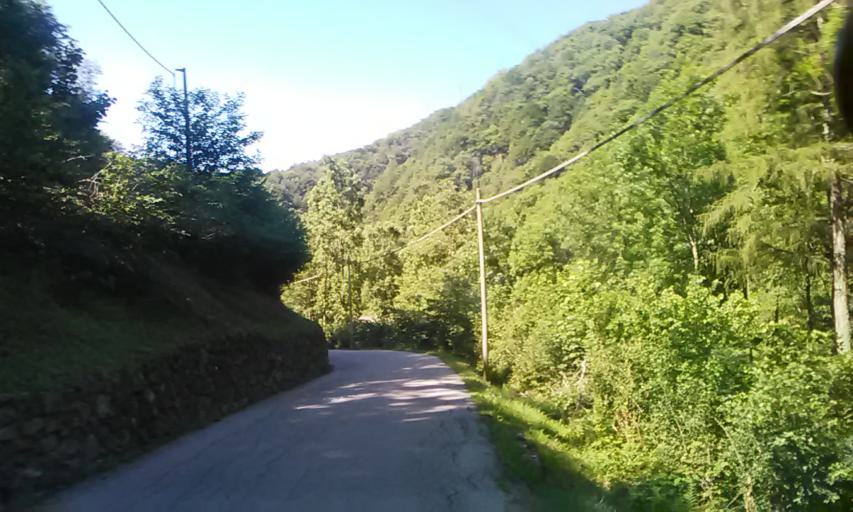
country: IT
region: Piedmont
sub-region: Provincia di Vercelli
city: Varallo
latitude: 45.8284
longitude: 8.2778
